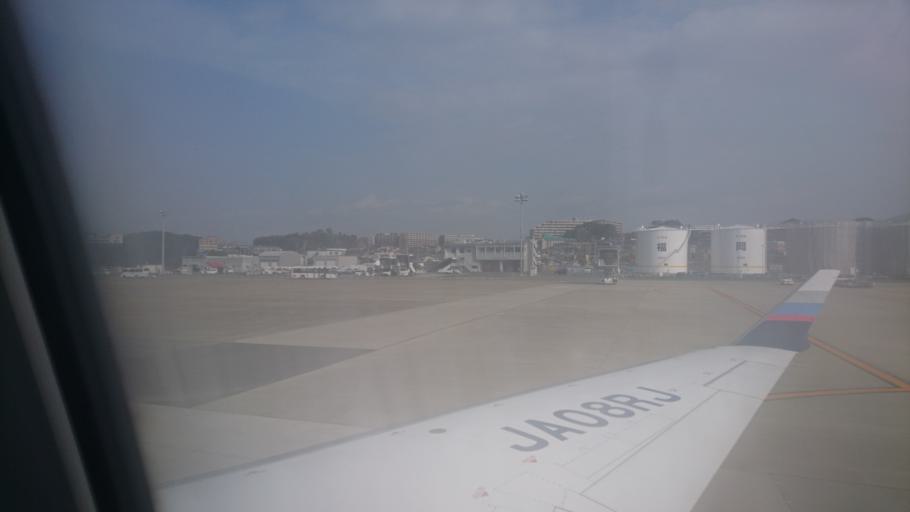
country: JP
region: Fukuoka
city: Fukuoka-shi
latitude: 33.5901
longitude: 130.4501
